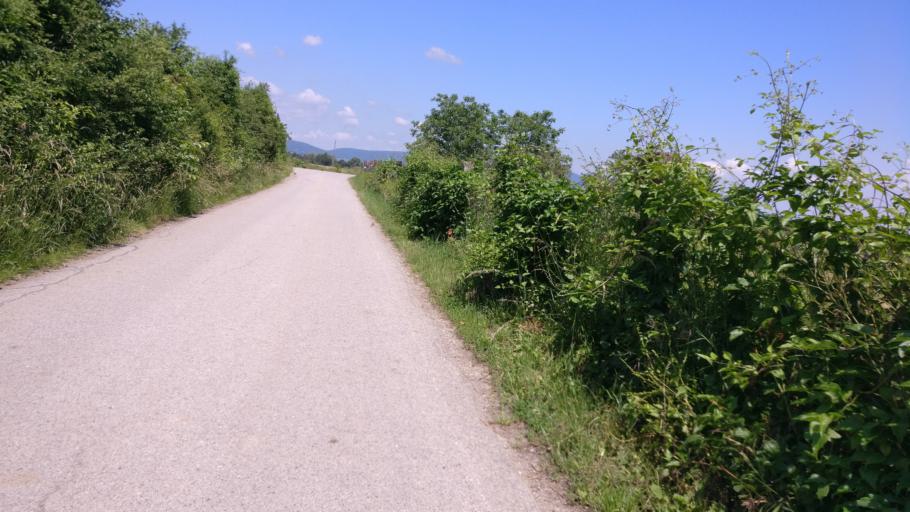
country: AT
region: Lower Austria
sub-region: Politischer Bezirk Baden
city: Tattendorf
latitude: 47.9576
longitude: 16.2956
